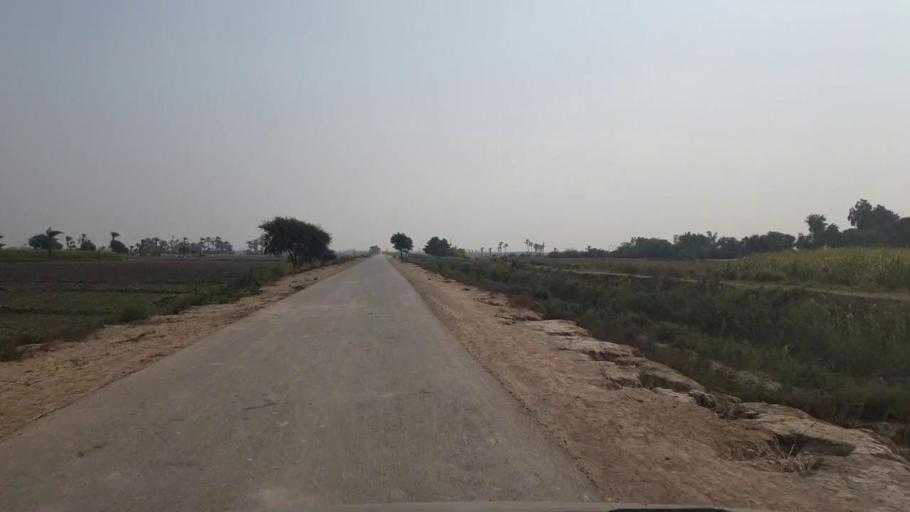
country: PK
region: Sindh
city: Tando Muhammad Khan
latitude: 25.1058
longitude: 68.3687
